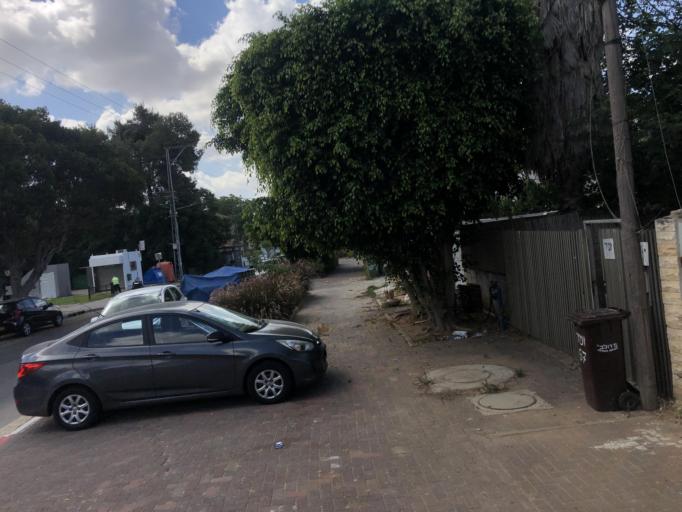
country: IL
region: Central District
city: Yehud
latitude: 32.0388
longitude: 34.8968
